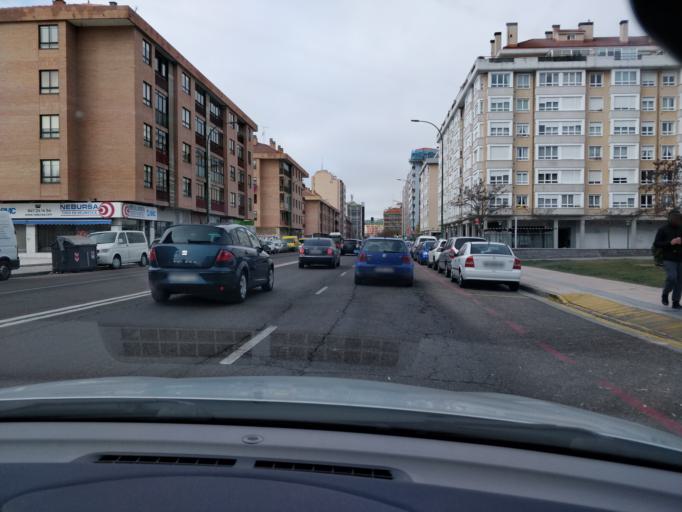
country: ES
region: Castille and Leon
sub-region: Provincia de Burgos
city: Burgos
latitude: 42.3478
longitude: -3.6708
